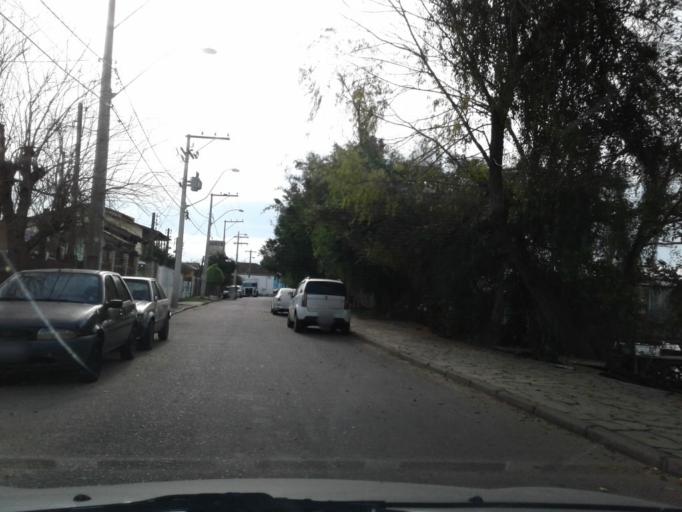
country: BR
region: Rio Grande do Sul
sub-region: Porto Alegre
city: Porto Alegre
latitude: -30.0157
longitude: -51.2581
